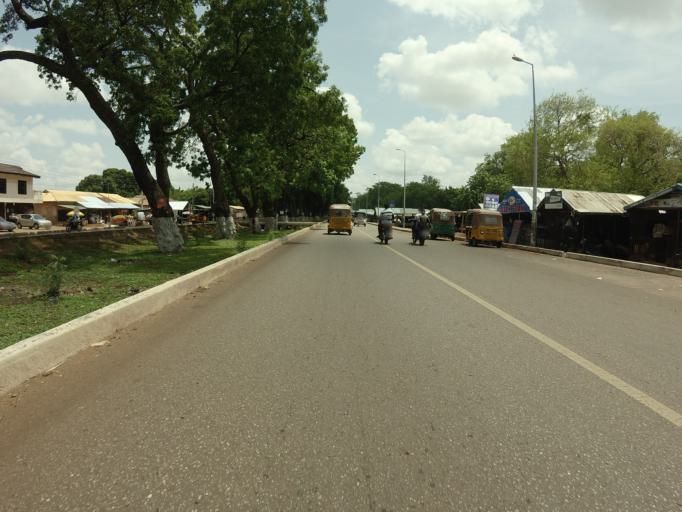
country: GH
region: Northern
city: Tamale
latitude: 9.4044
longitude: -0.8550
